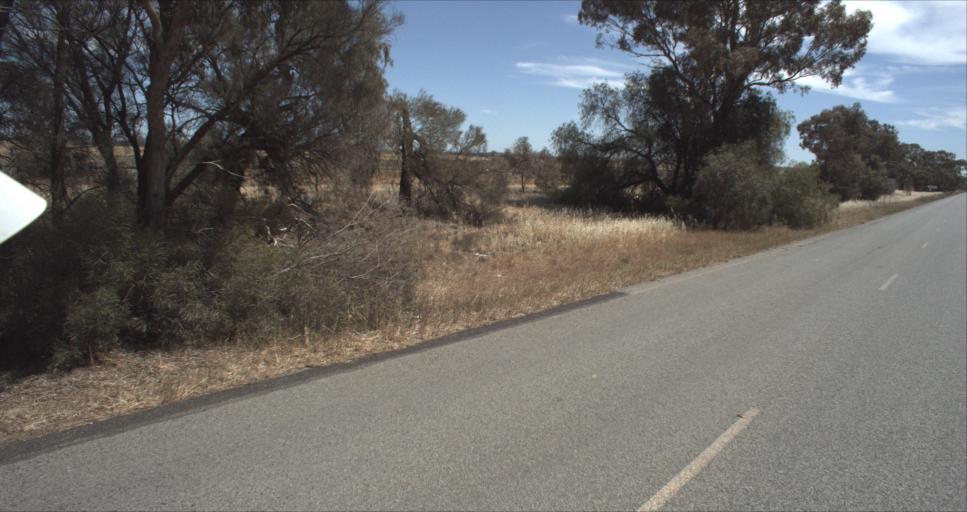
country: AU
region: New South Wales
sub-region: Leeton
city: Leeton
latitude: -34.6441
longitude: 146.4698
